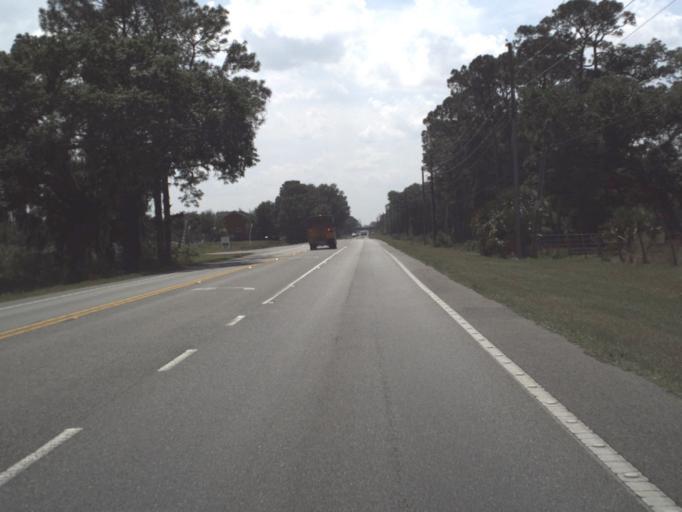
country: US
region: Florida
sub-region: Lake County
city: Howie In The Hills
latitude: 28.6537
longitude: -81.7931
